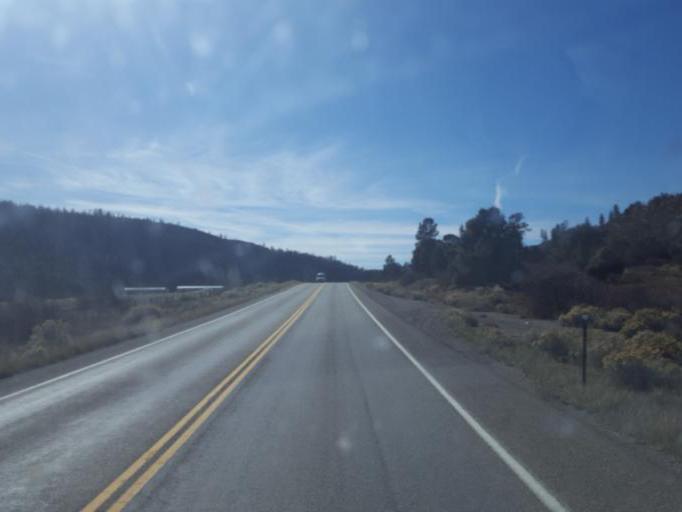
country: US
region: Colorado
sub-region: Archuleta County
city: Pagosa Springs
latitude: 37.2180
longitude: -107.2232
